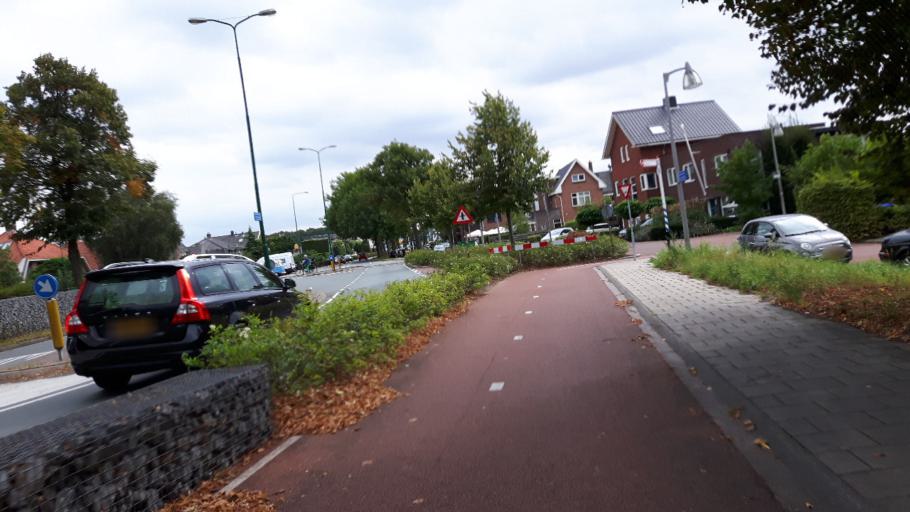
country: NL
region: Utrecht
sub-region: Stichtse Vecht
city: Maarssen
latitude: 52.1345
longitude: 5.0430
